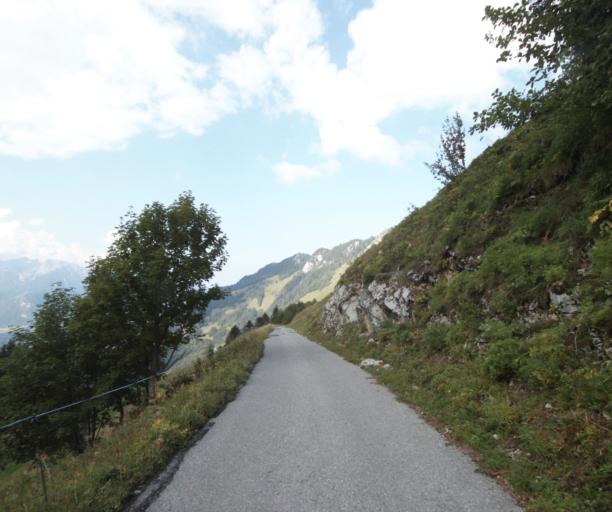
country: CH
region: Vaud
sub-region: Riviera-Pays-d'Enhaut District
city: Caux
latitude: 46.4218
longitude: 6.9929
